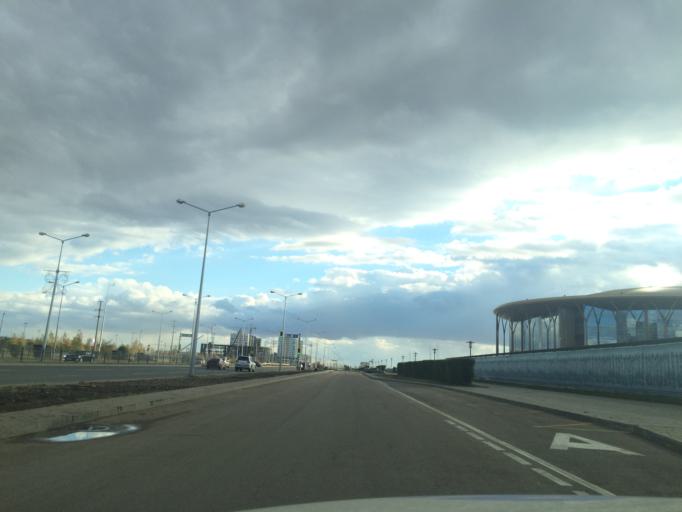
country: KZ
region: Astana Qalasy
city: Astana
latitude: 51.1117
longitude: 71.3987
